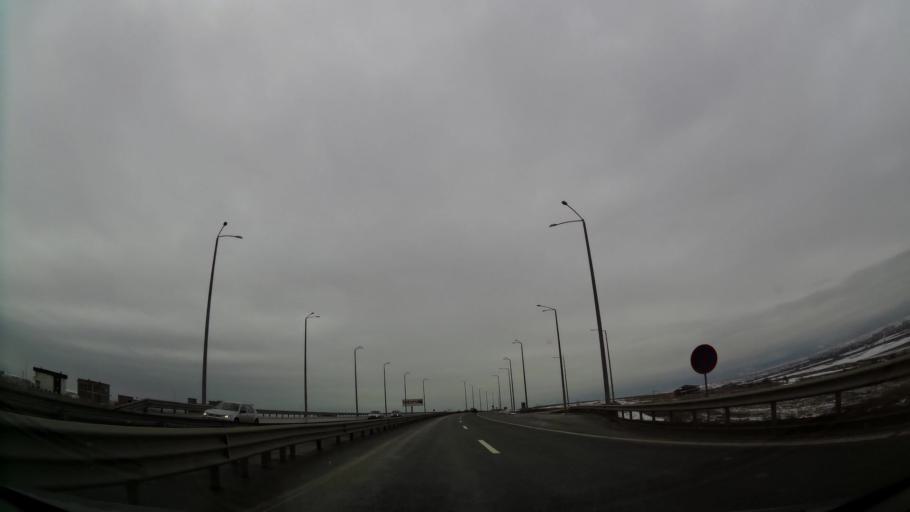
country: XK
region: Pristina
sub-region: Kosovo Polje
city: Kosovo Polje
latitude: 42.6286
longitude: 21.1347
